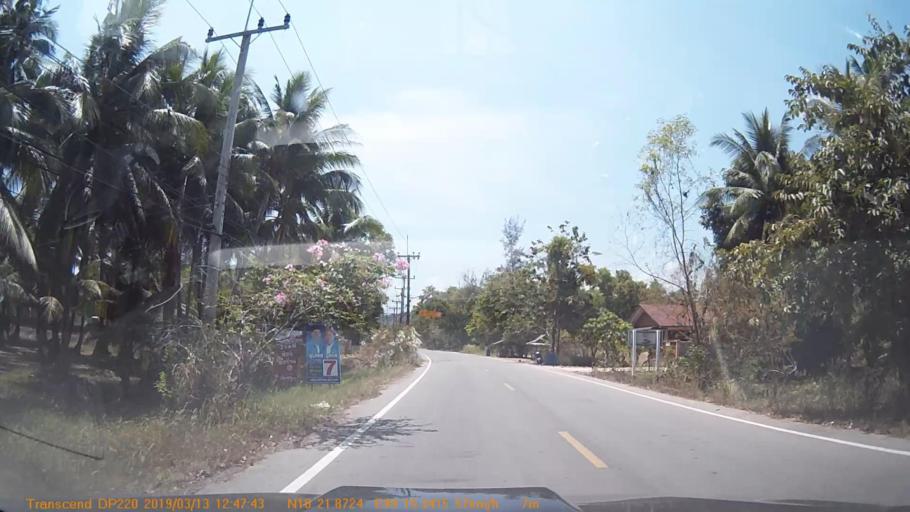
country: TH
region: Chumphon
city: Chumphon
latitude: 10.3645
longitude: 99.2553
